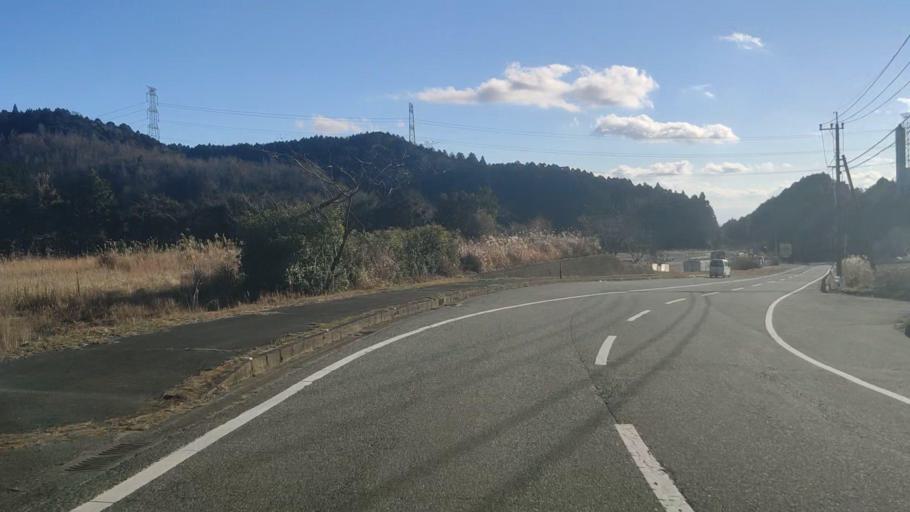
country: JP
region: Saga Prefecture
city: Kanzakimachi-kanzaki
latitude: 33.4020
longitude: 130.2725
